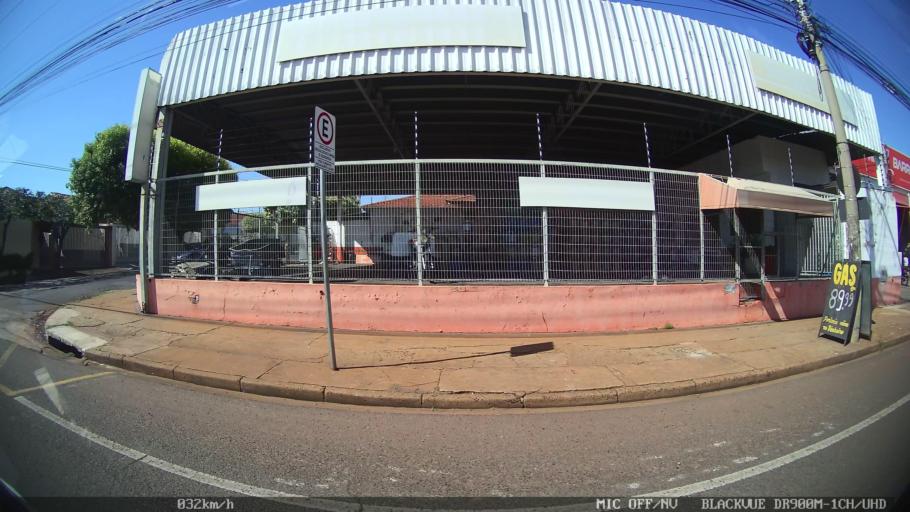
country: BR
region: Sao Paulo
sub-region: Sao Jose Do Rio Preto
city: Sao Jose do Rio Preto
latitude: -20.8041
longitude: -49.4001
